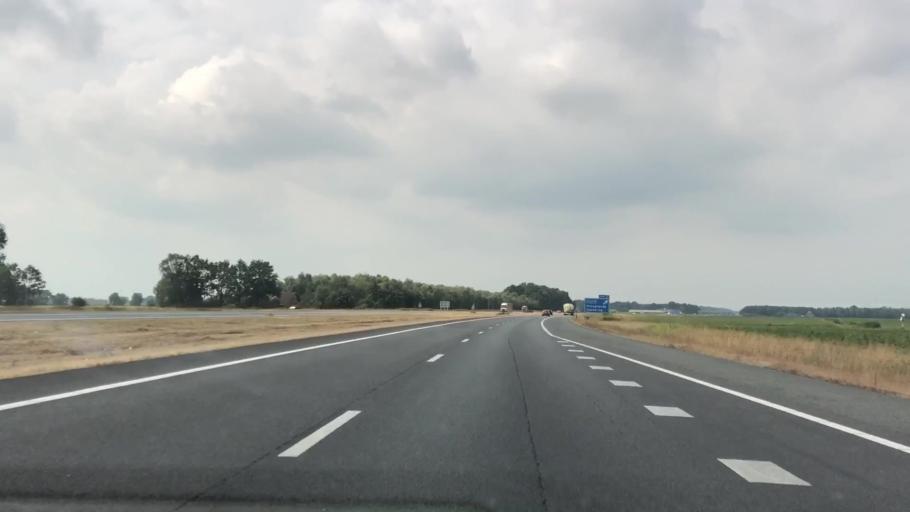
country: NL
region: Drenthe
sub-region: Gemeente Coevorden
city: Coevorden
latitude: 52.7130
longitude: 6.6323
